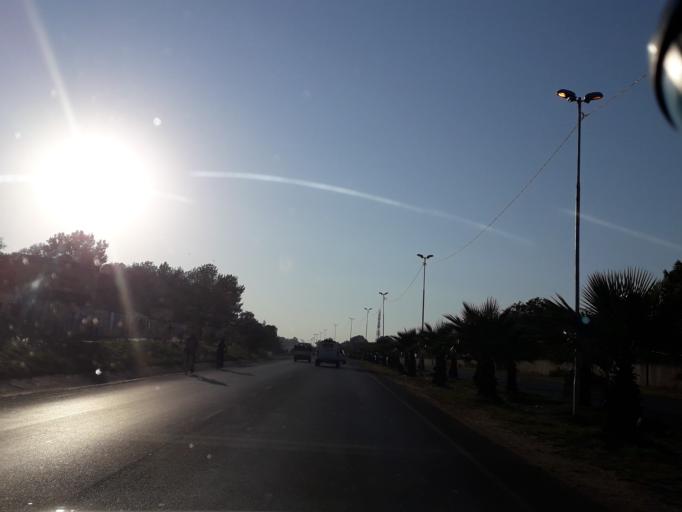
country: ZA
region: Gauteng
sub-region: West Rand District Municipality
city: Muldersdriseloop
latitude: -26.0725
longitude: 27.9159
